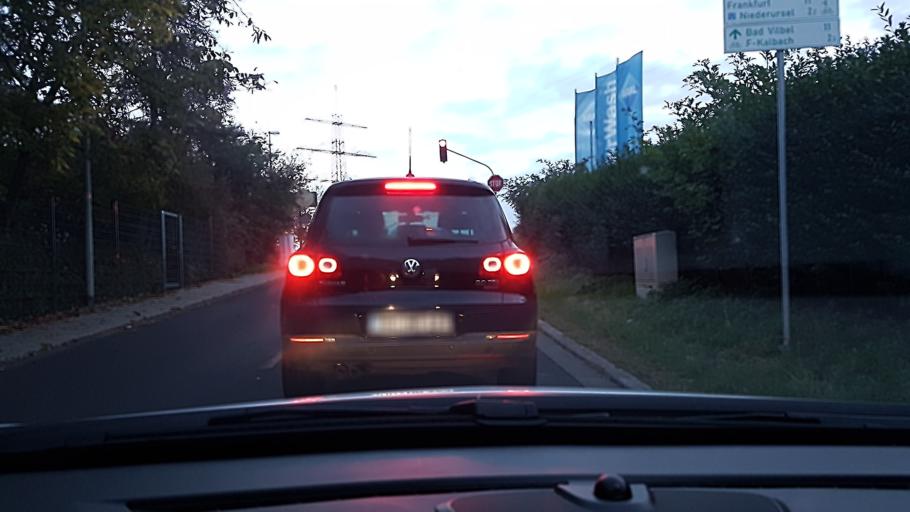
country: DE
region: Hesse
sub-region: Regierungsbezirk Darmstadt
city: Steinbach am Taunus
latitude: 50.1806
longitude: 8.6048
